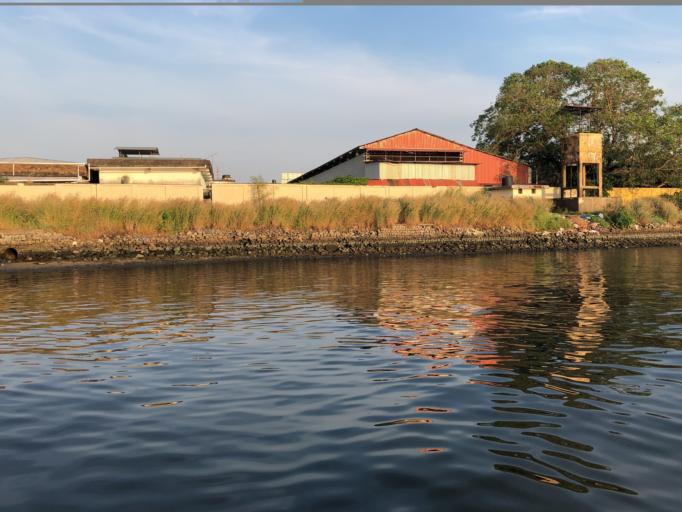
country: IN
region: Karnataka
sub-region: Dakshina Kannada
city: Mangalore
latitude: 12.8663
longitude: 74.8306
